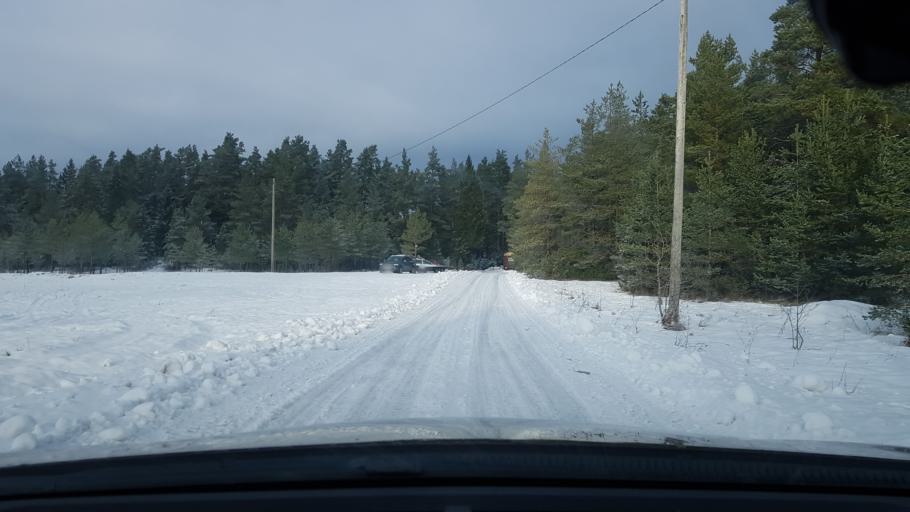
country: EE
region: Harju
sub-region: Keila linn
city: Keila
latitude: 59.2909
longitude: 24.2613
